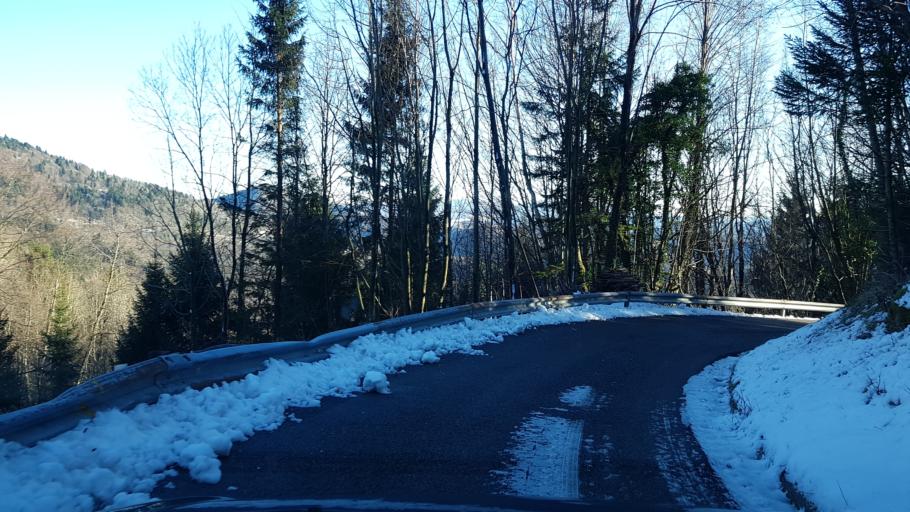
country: IT
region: Friuli Venezia Giulia
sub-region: Provincia di Udine
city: Savogna
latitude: 46.1908
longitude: 13.5295
